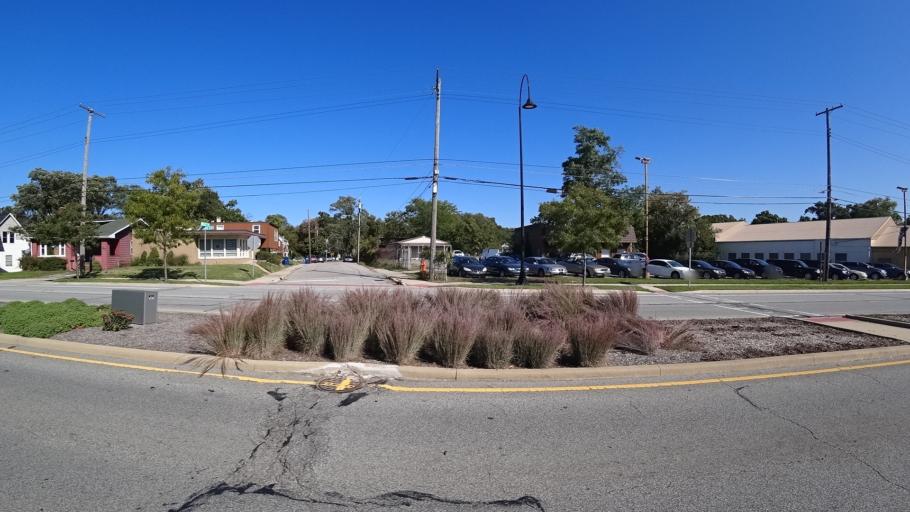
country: US
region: Indiana
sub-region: LaPorte County
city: Michigan City
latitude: 41.7121
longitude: -86.8834
